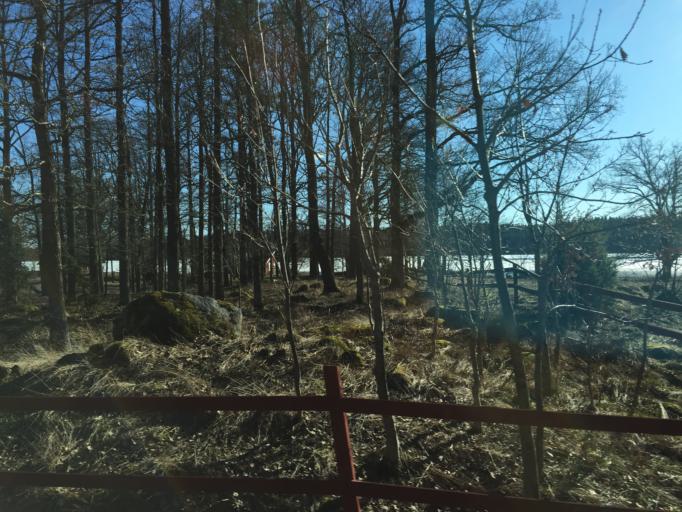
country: SE
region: Soedermanland
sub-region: Vingakers Kommun
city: Vingaker
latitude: 58.9356
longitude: 15.8594
